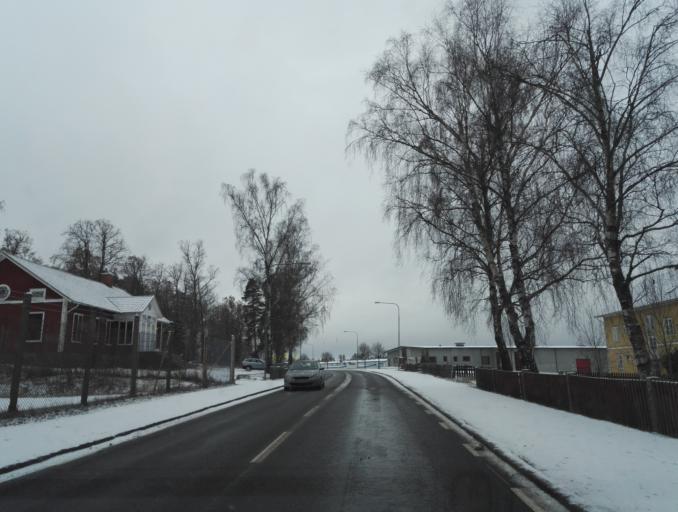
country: SE
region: Kronoberg
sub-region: Lessebo Kommun
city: Lessebo
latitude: 56.7469
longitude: 15.2695
